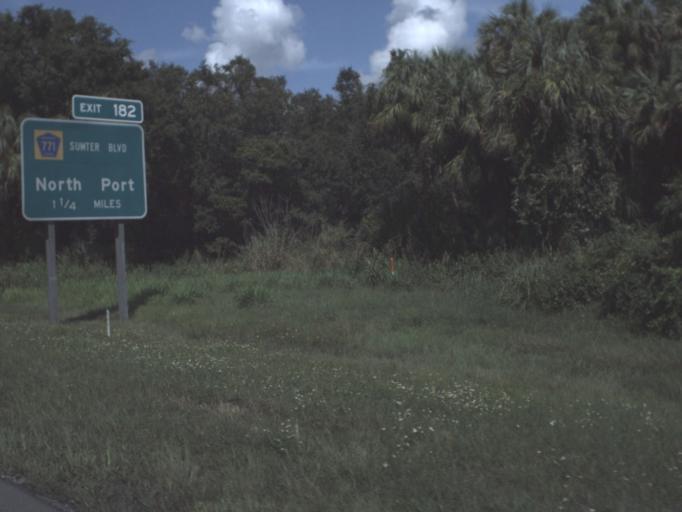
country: US
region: Florida
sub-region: Sarasota County
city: North Port
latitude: 27.0993
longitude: -82.1776
